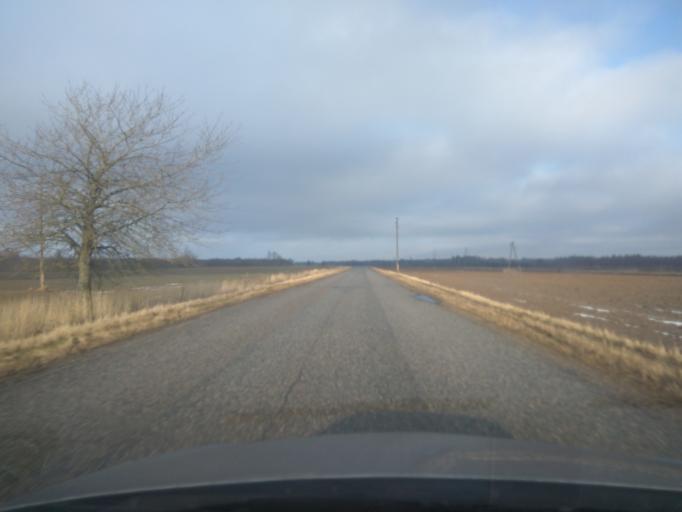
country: LV
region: Saldus Rajons
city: Saldus
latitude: 56.7653
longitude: 22.3862
